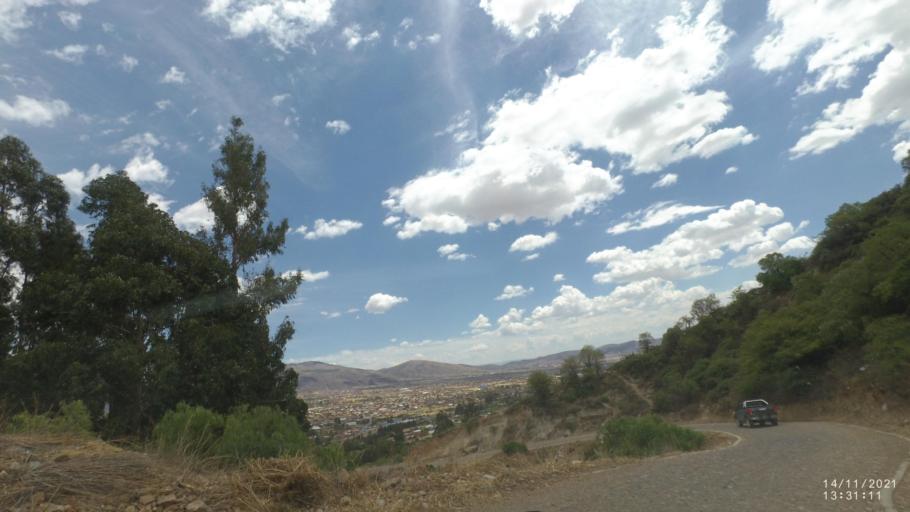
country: BO
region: Cochabamba
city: Colomi
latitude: -17.3947
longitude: -65.9808
